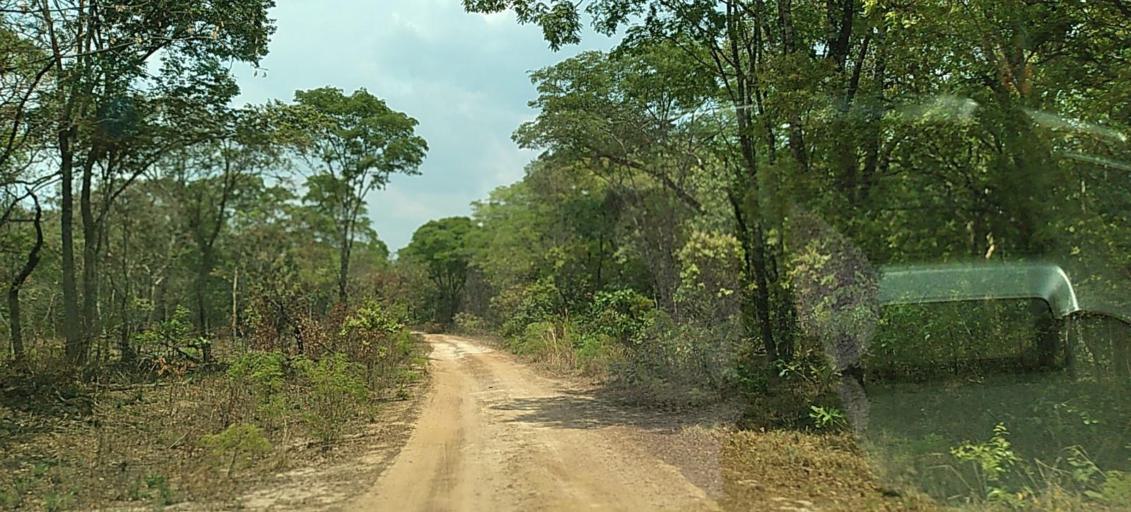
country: ZM
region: Copperbelt
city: Chingola
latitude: -12.7897
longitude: 27.6570
